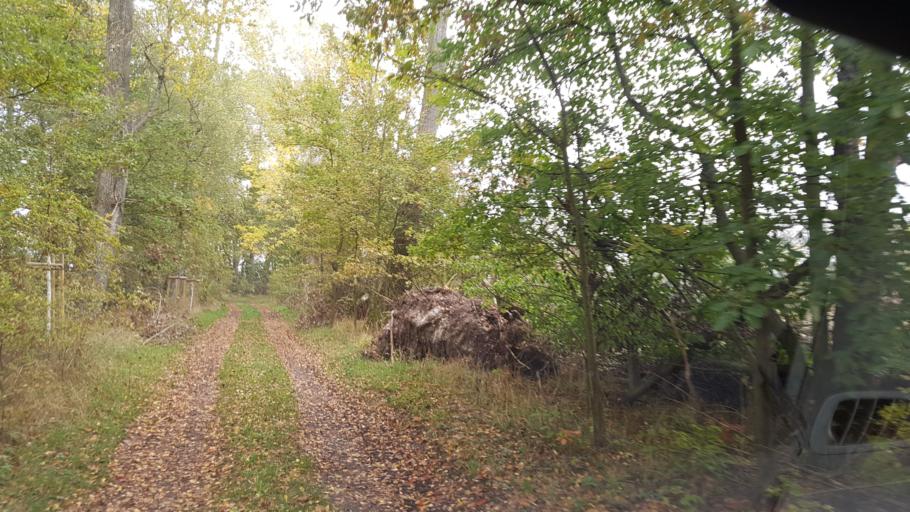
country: DE
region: Brandenburg
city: Schonewalde
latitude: 51.6962
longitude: 13.6058
